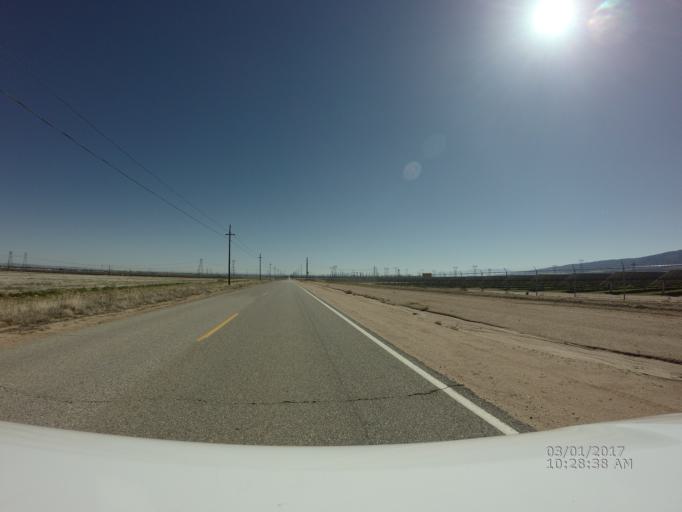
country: US
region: California
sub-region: Los Angeles County
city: Leona Valley
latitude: 34.6891
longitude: -118.3170
